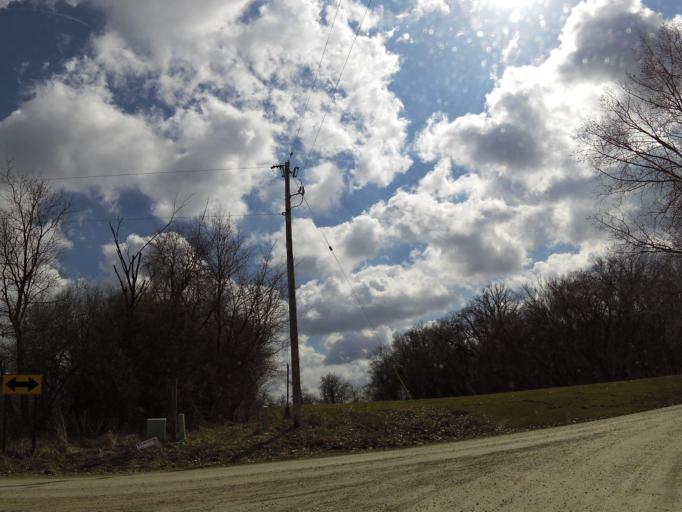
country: US
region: Minnesota
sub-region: Dodge County
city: Mantorville
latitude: 44.0680
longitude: -92.7183
